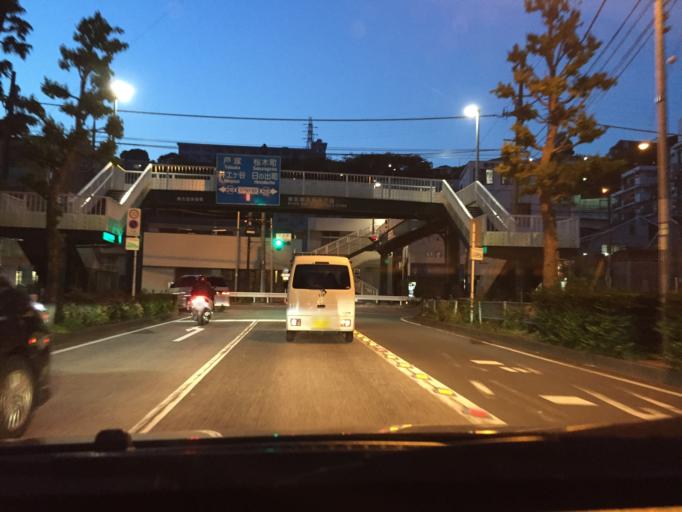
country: JP
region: Kanagawa
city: Yokohama
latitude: 35.4352
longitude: 139.6106
